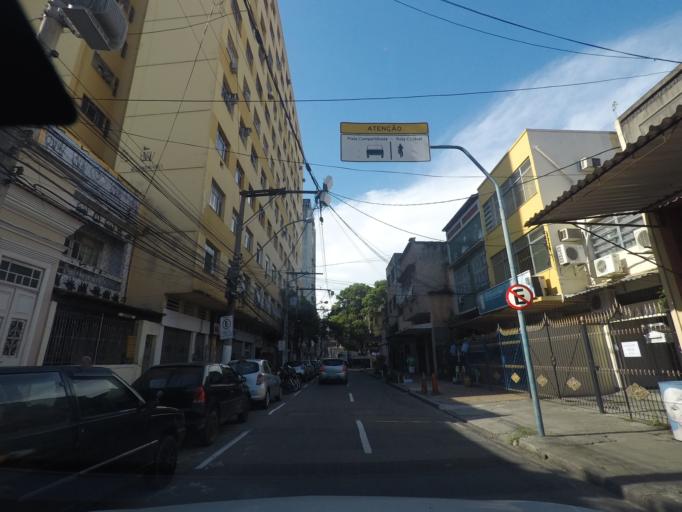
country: BR
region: Rio de Janeiro
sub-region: Niteroi
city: Niteroi
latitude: -22.8864
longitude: -43.1222
